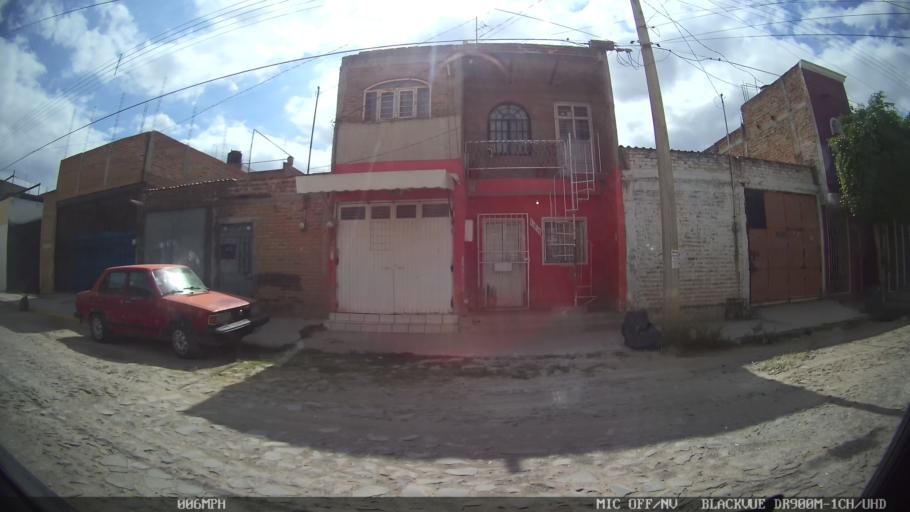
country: MX
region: Jalisco
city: Tonala
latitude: 20.6703
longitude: -103.2522
